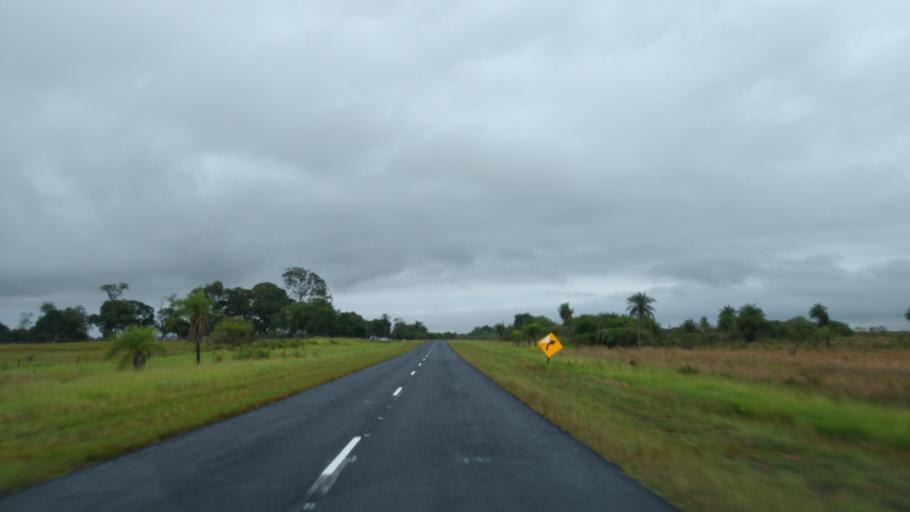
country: AR
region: Corrientes
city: Loreto
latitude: -27.7105
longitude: -57.2284
